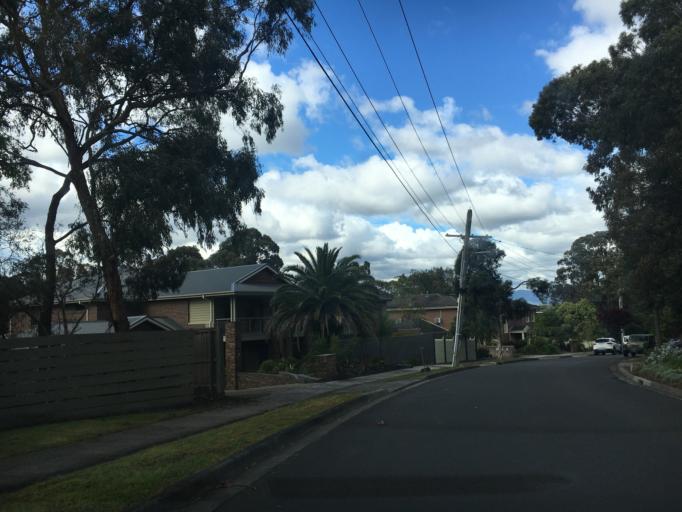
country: AU
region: Victoria
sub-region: Whitehorse
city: Vermont South
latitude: -37.8683
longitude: 145.1734
